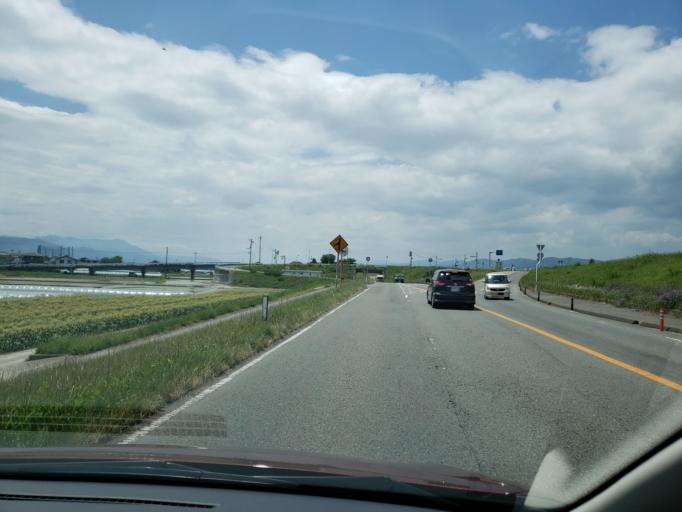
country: JP
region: Tokushima
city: Ishii
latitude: 34.1011
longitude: 134.4406
